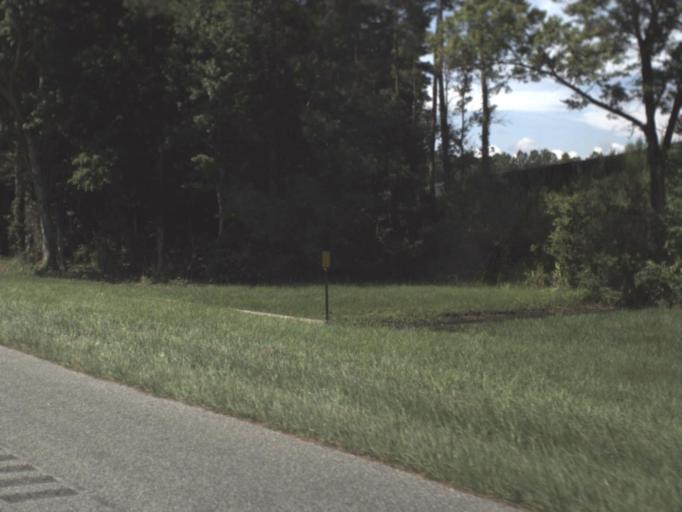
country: US
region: Florida
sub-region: Saint Johns County
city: Palm Valley
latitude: 30.0135
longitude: -81.4785
